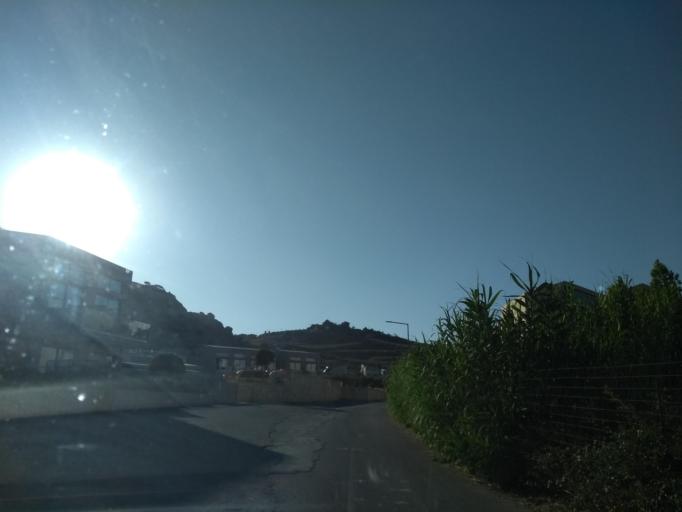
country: GR
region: Crete
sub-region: Nomos Chanias
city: Kalivai
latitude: 35.4653
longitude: 24.1558
